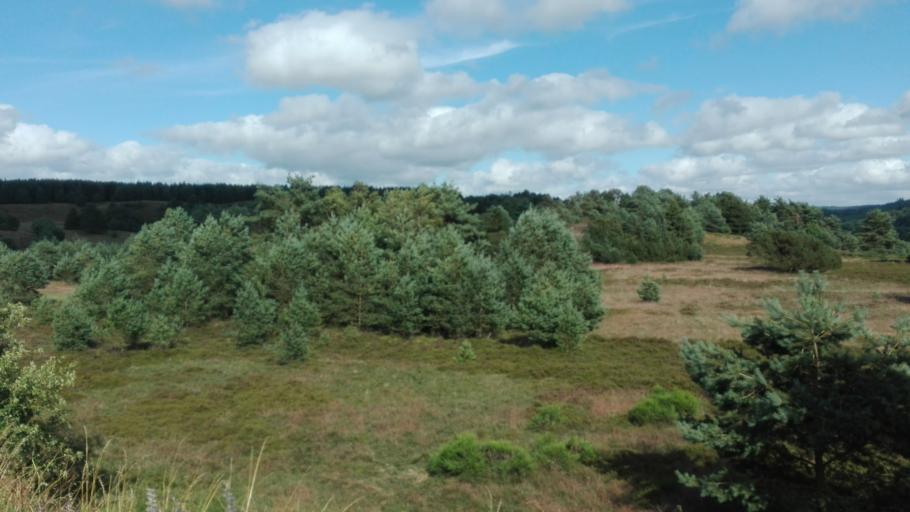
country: DK
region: Central Jutland
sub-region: Silkeborg Kommune
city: Virklund
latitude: 56.0521
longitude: 9.4721
